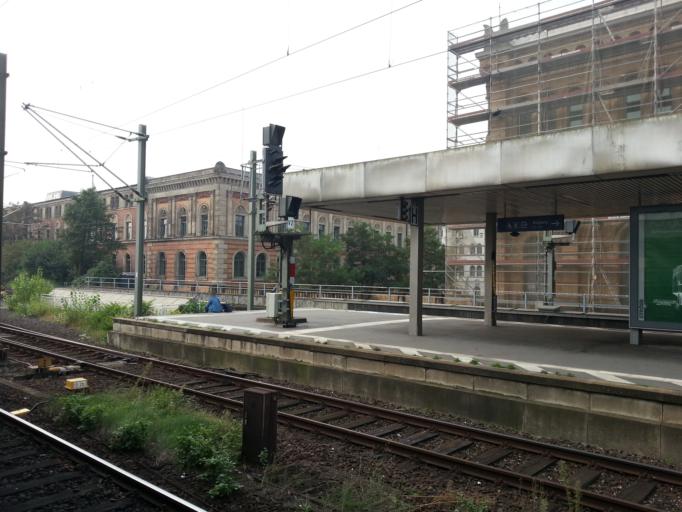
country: DE
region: Lower Saxony
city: Hannover
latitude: 52.3763
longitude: 9.7421
